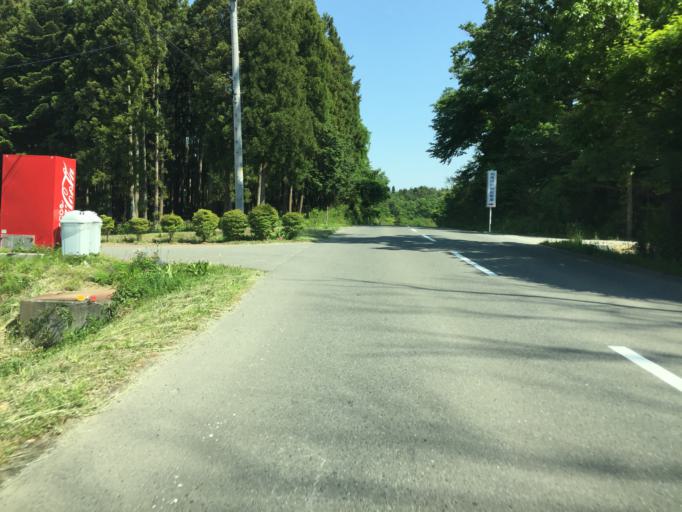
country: JP
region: Miyagi
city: Marumori
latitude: 37.8203
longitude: 140.8793
